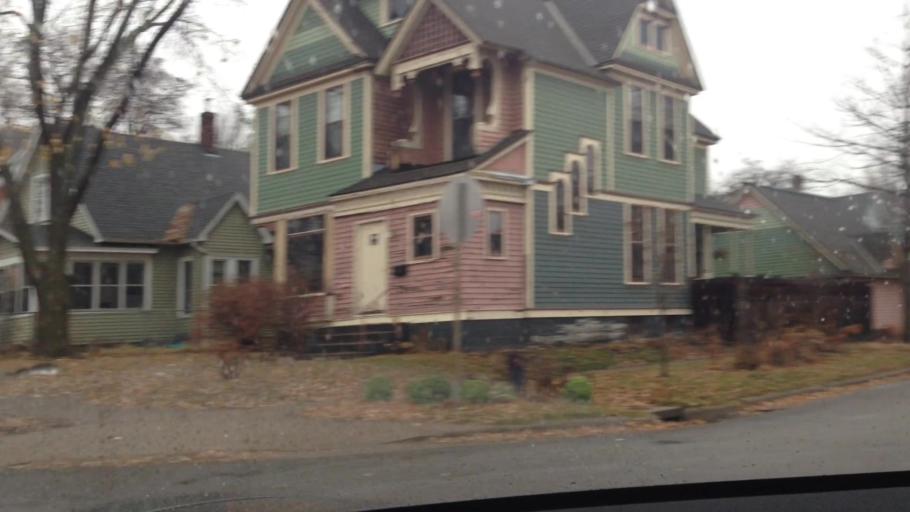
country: US
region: Minnesota
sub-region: Ramsey County
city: Saint Paul
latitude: 44.9702
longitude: -93.0773
